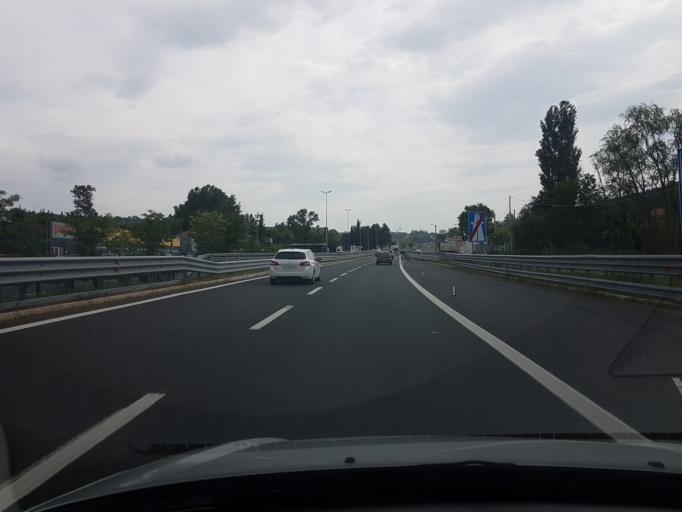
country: SI
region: Koper-Capodistria
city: Spodnje Skofije
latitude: 45.5848
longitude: 13.7978
